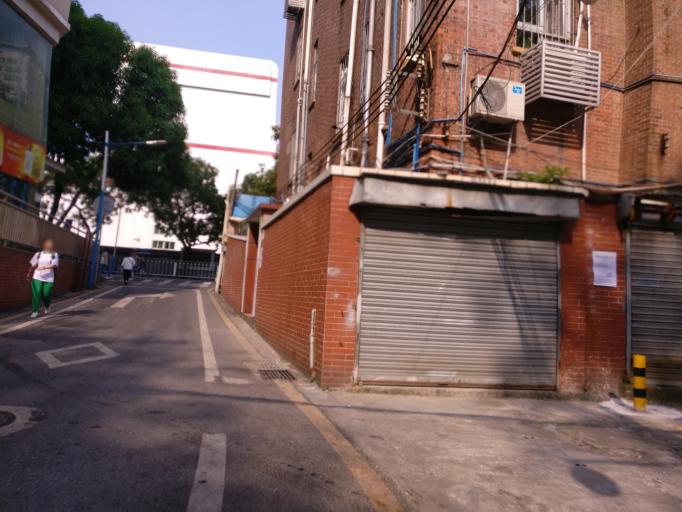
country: CN
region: Guangdong
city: Guangzhou
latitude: 23.1242
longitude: 113.2960
